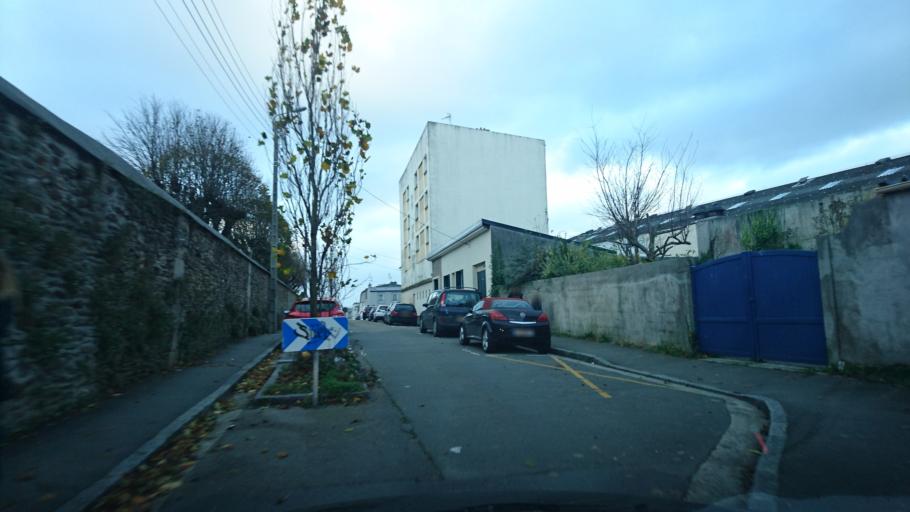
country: FR
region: Brittany
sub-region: Departement du Finistere
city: Brest
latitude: 48.3933
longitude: -4.4786
